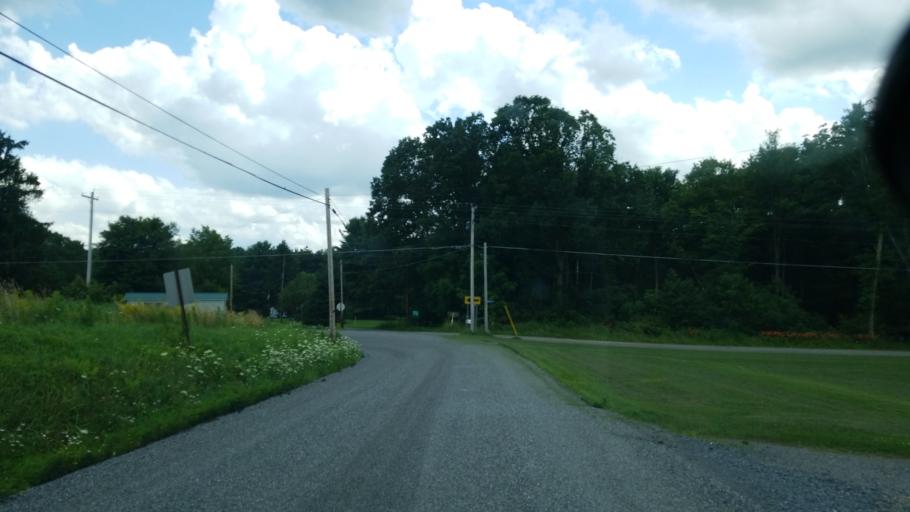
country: US
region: Pennsylvania
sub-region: Jefferson County
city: Brookville
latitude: 41.2327
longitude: -79.0116
